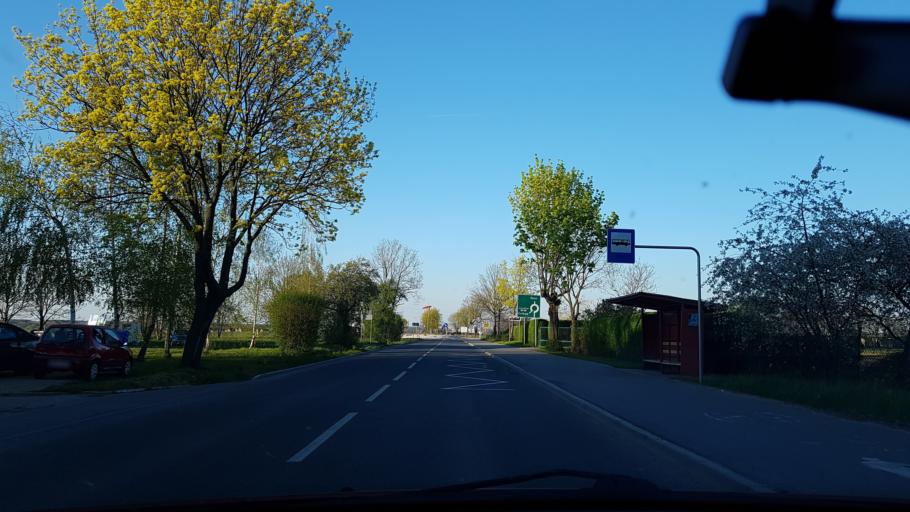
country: PL
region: Opole Voivodeship
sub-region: Powiat nyski
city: Nysa
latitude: 50.4383
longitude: 17.3092
